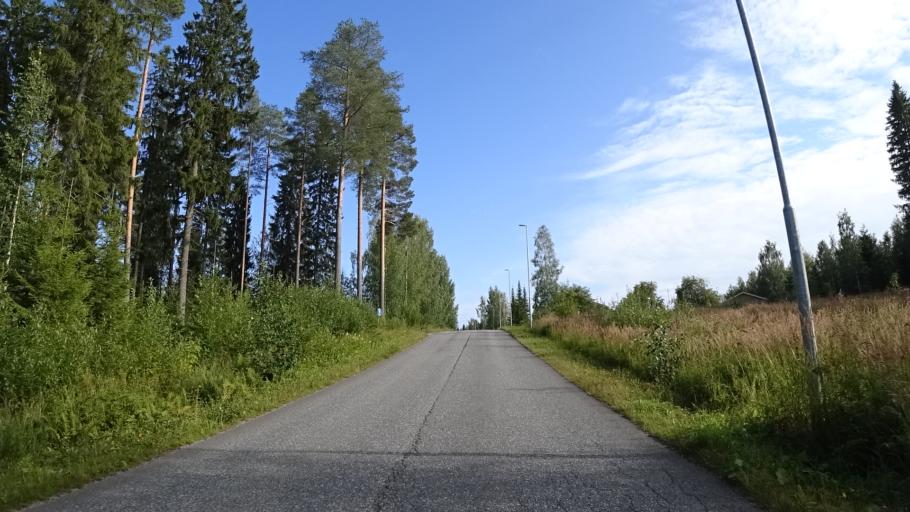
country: FI
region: North Karelia
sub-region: Joensuu
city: Eno
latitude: 62.7963
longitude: 30.1388
